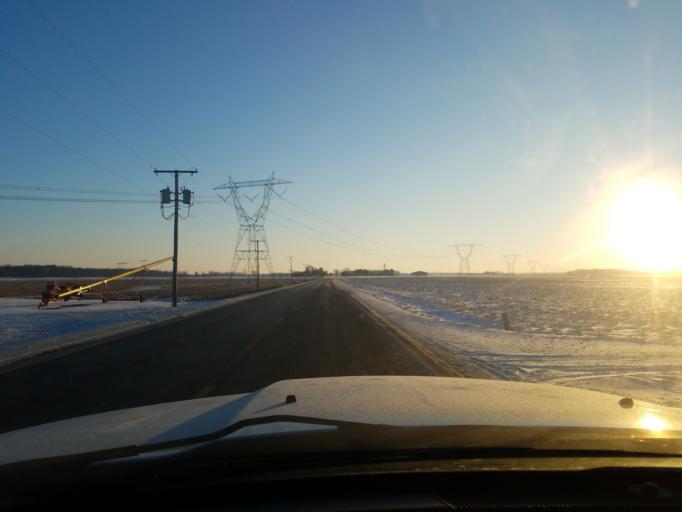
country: US
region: Indiana
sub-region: Marshall County
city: Bremen
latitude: 41.4499
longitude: -86.2321
